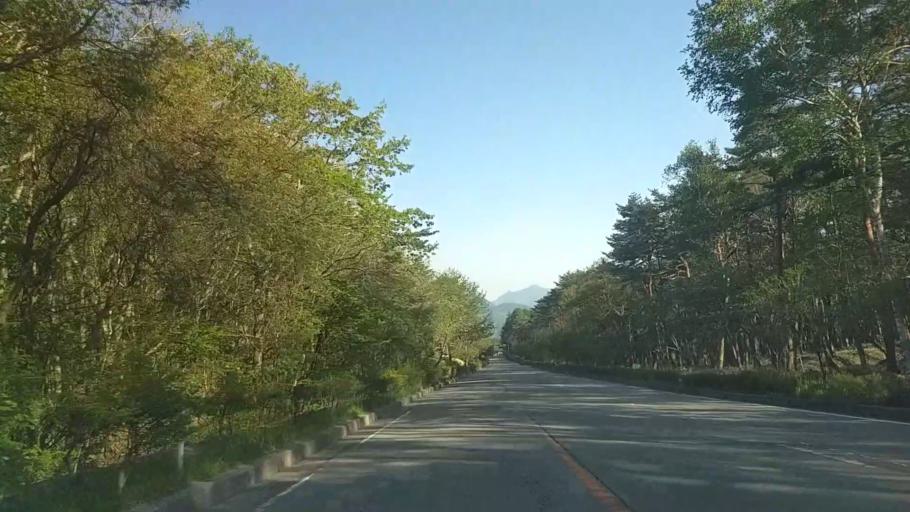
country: JP
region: Yamanashi
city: Nirasaki
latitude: 35.9285
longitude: 138.4296
